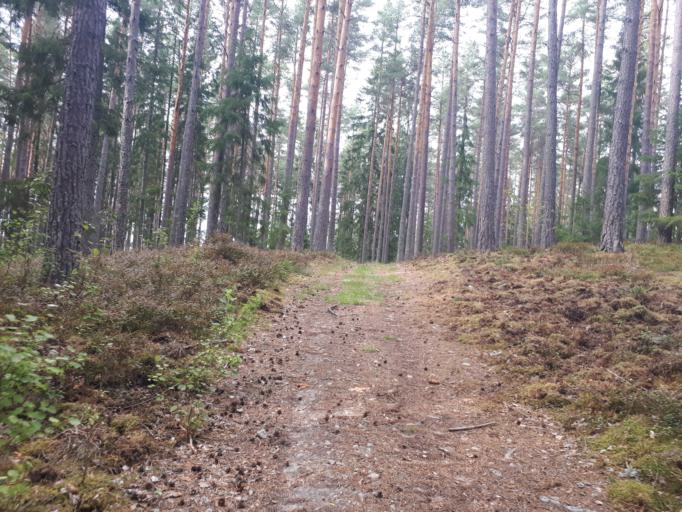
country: SE
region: Soedermanland
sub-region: Flens Kommun
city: Halleforsnas
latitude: 59.0688
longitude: 16.3931
